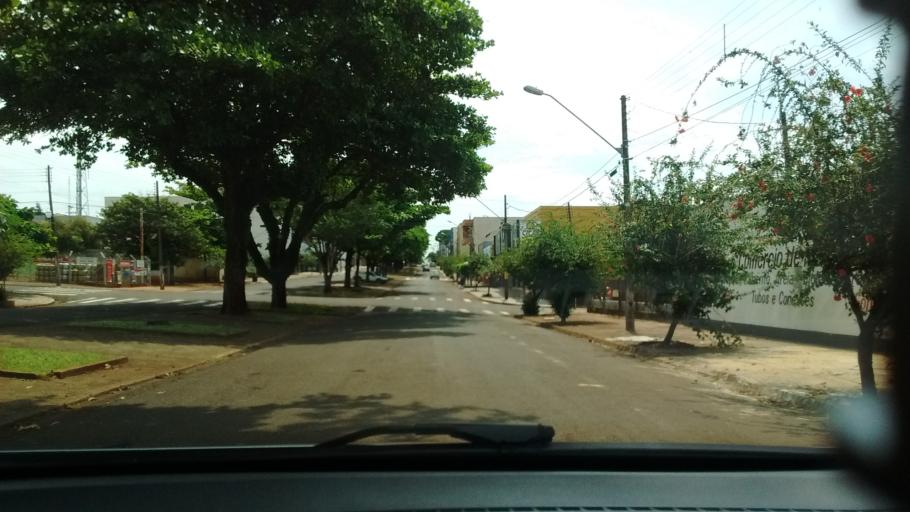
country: BR
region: Parana
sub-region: Corbelia
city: Corbelia
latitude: -24.5423
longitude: -52.9863
